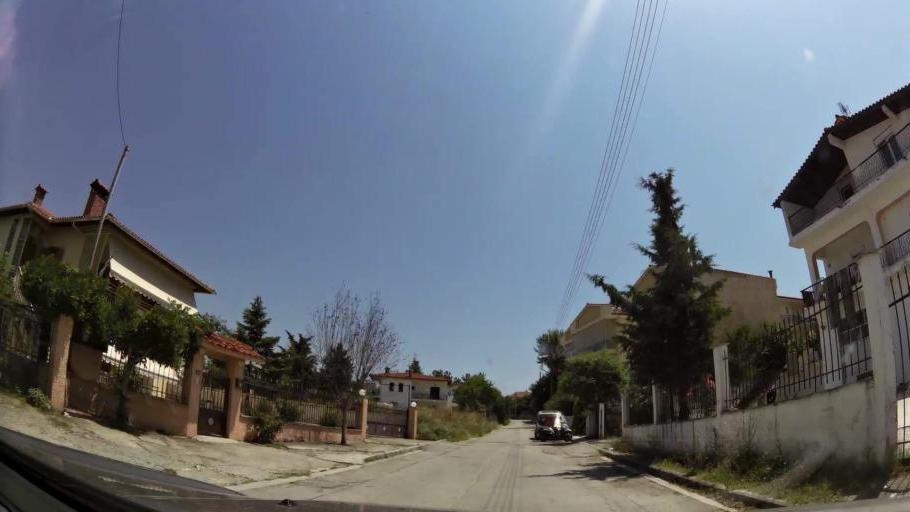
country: GR
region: Central Macedonia
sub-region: Nomos Thessalonikis
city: Trilofos
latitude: 40.4713
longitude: 22.9726
